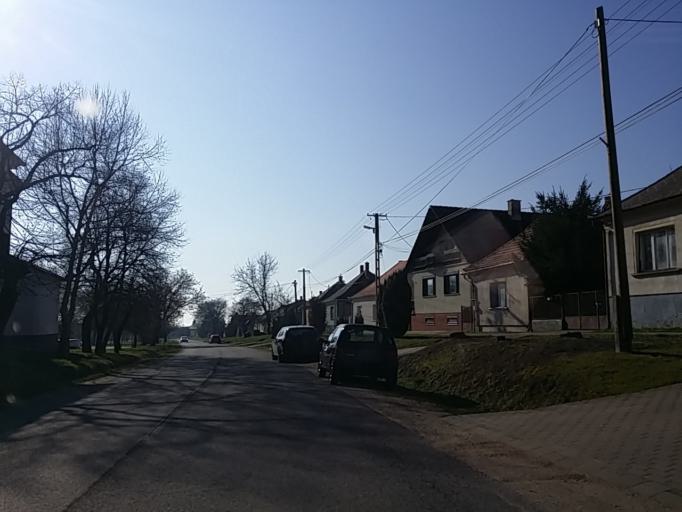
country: HU
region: Fejer
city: Szarliget
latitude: 47.4767
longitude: 18.5191
